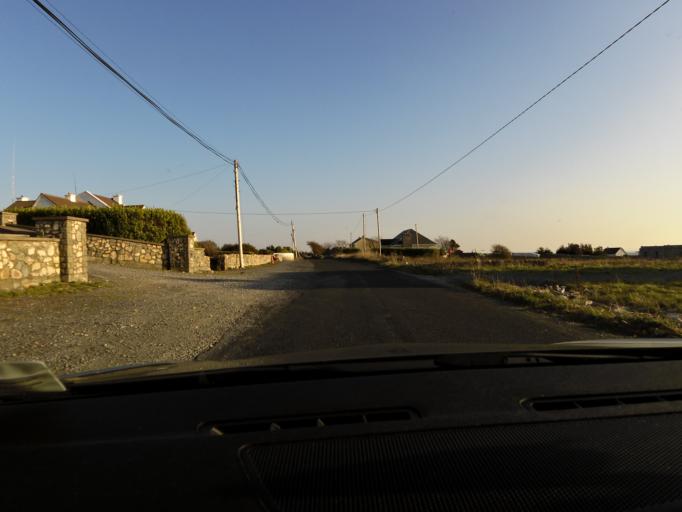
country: IE
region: Connaught
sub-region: County Galway
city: Oughterard
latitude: 53.2531
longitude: -9.5420
